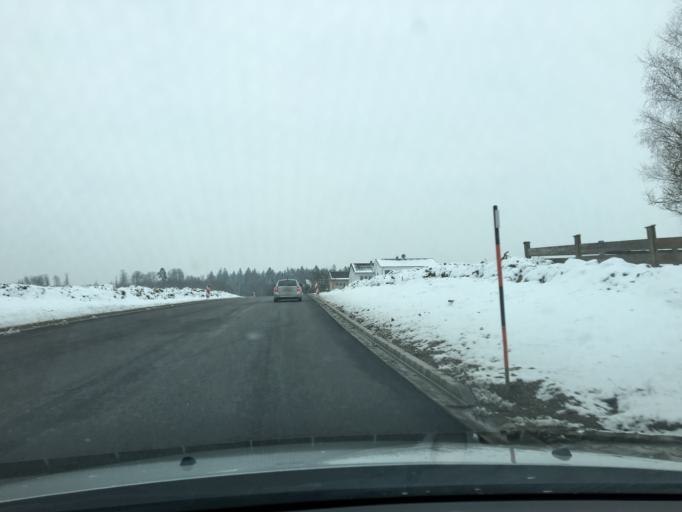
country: DE
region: Bavaria
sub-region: Upper Bavaria
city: Egglkofen
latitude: 48.4018
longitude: 12.4456
